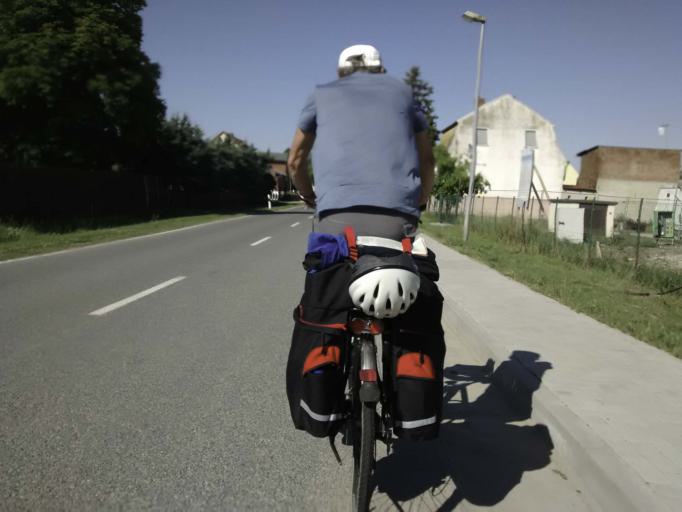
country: DE
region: Saxony-Anhalt
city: Gross Rosenburg
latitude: 51.9218
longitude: 11.9468
